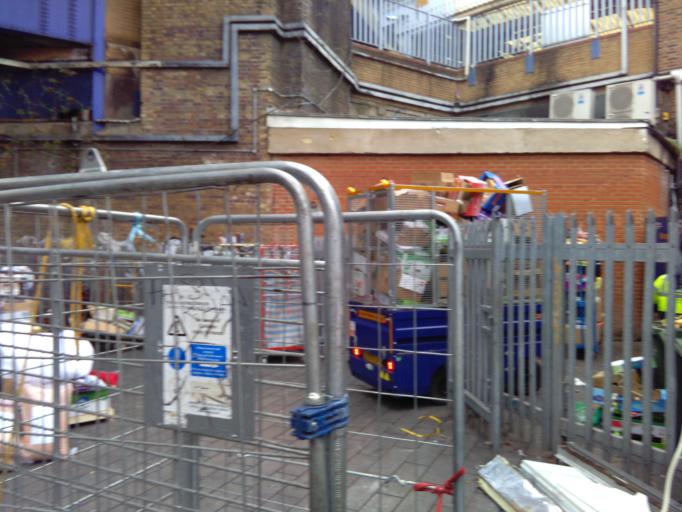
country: GB
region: England
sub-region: Greater London
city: Brixton
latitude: 51.4628
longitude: -0.1127
